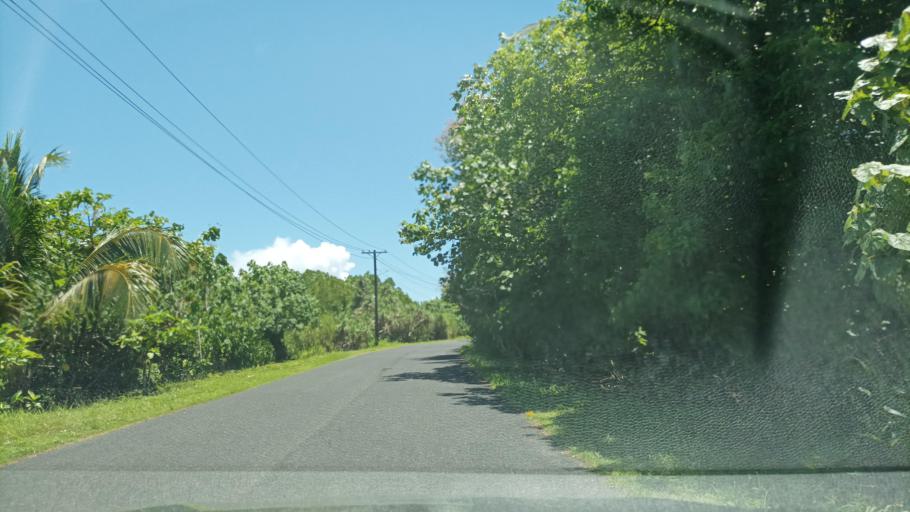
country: FM
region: Pohnpei
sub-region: Kolonia Municipality
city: Kolonia
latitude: 6.9681
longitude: 158.2517
